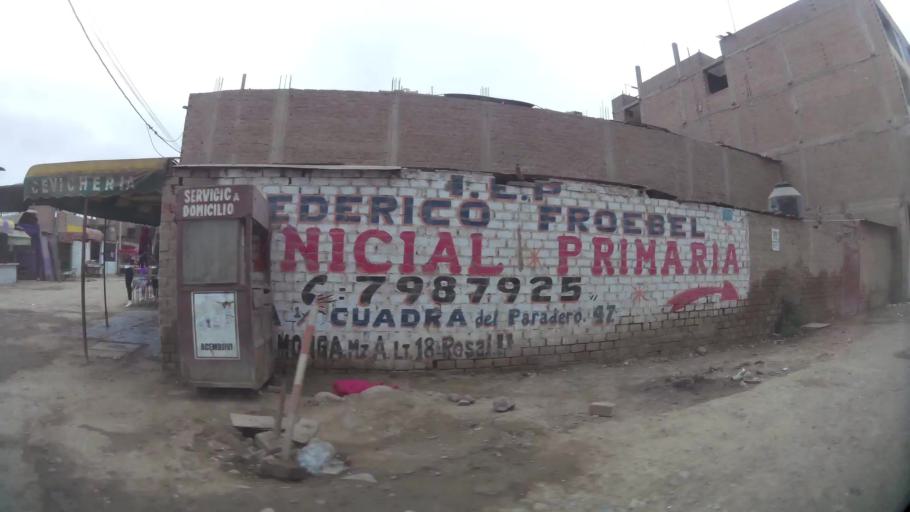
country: PE
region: Lima
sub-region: Lima
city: Independencia
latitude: -11.9593
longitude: -77.0961
